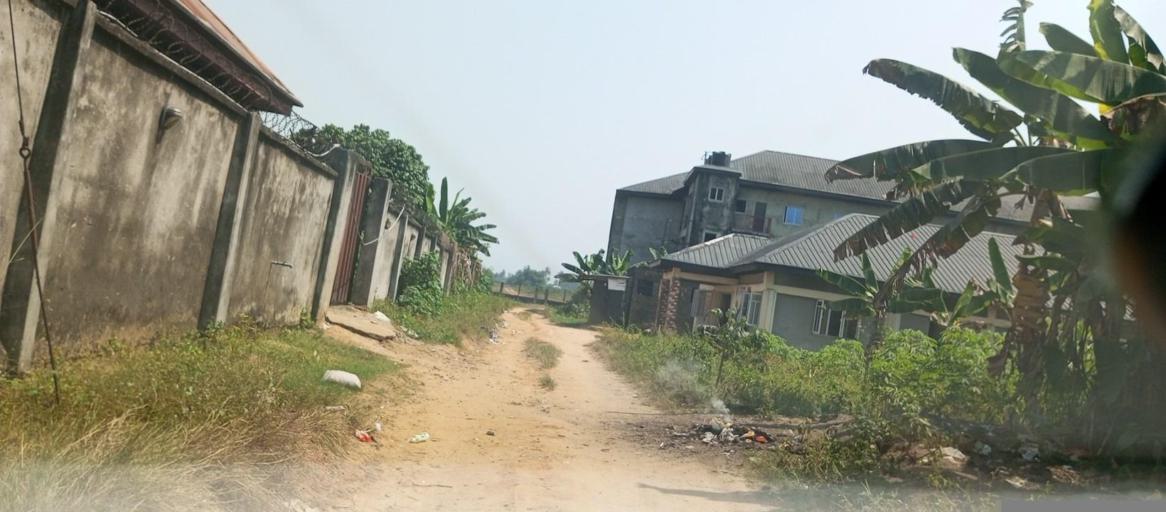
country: NG
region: Rivers
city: Emuoha
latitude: 4.9180
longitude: 6.9201
